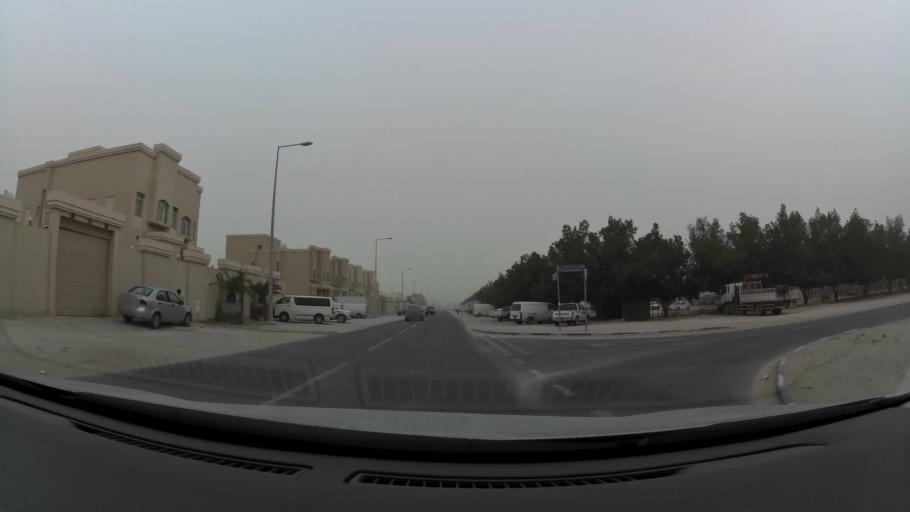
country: QA
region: Baladiyat ad Dawhah
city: Doha
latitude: 25.2431
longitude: 51.4813
